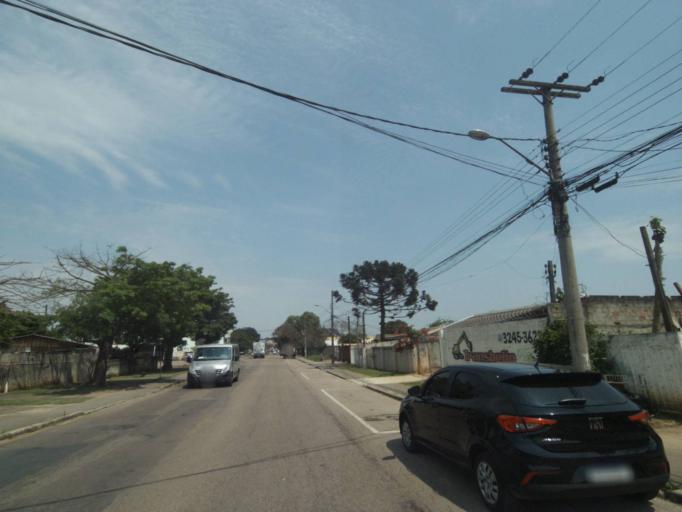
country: BR
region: Parana
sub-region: Curitiba
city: Curitiba
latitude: -25.4799
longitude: -49.3294
